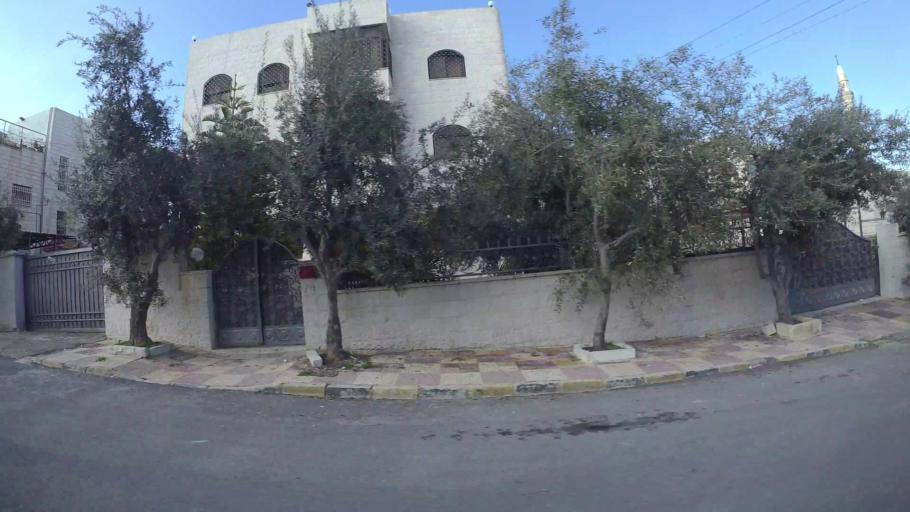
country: JO
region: Amman
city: Al Bunayyat ash Shamaliyah
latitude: 31.8993
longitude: 35.9179
